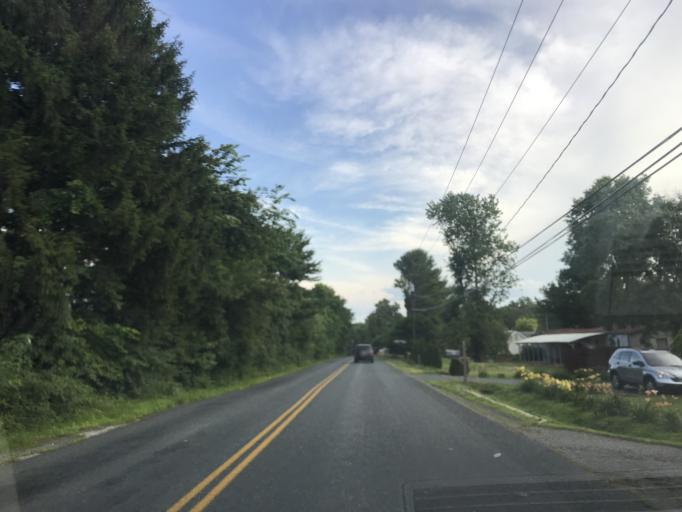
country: US
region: Maryland
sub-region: Harford County
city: Perryman
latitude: 39.4944
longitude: -76.2105
